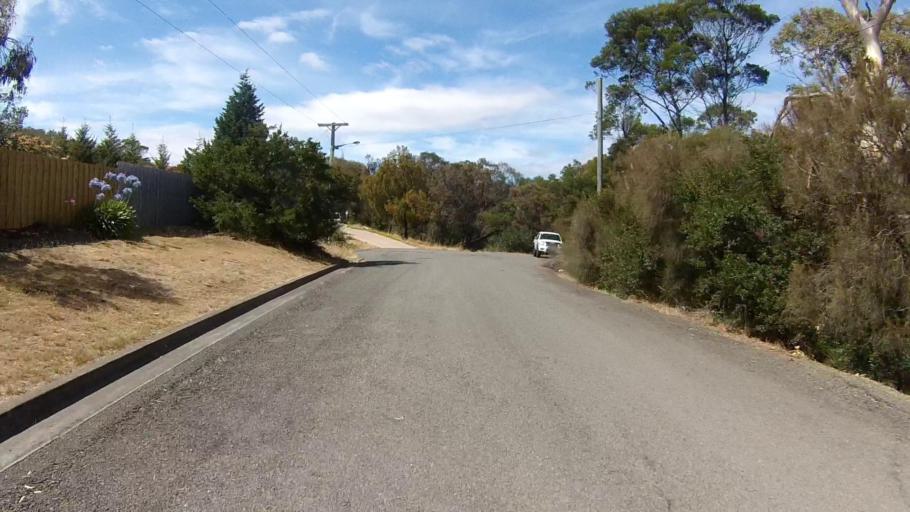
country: AU
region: Tasmania
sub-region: Glenorchy
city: Lutana
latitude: -42.8262
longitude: 147.3206
